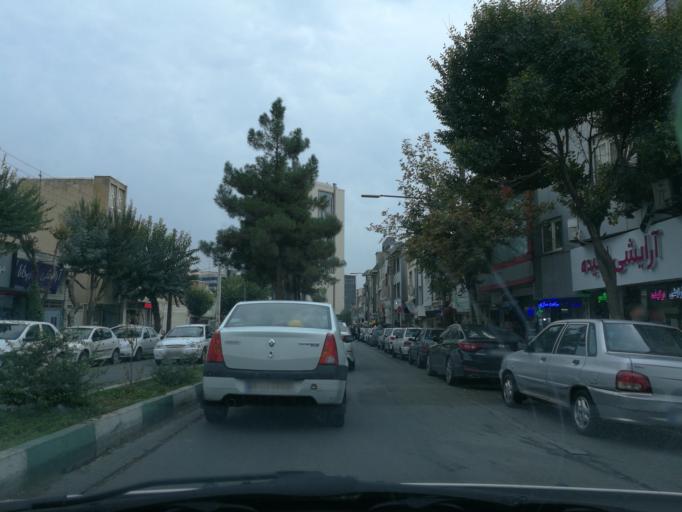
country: IR
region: Alborz
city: Karaj
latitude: 35.8456
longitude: 50.9703
